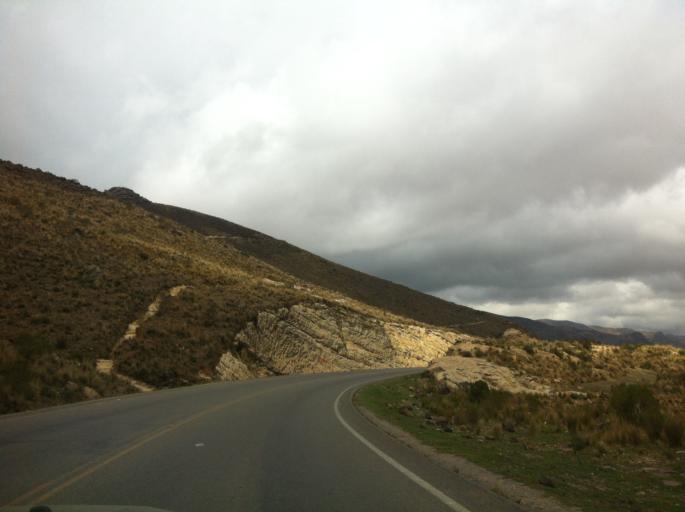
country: BO
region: Cochabamba
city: Irpa Irpa
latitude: -17.7017
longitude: -66.4837
